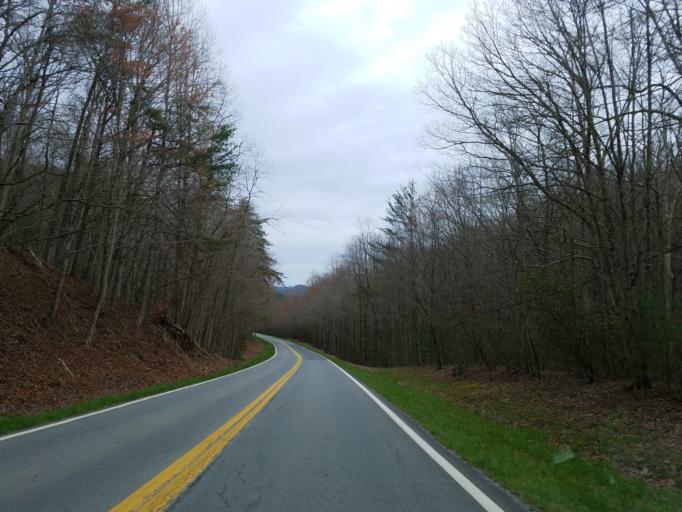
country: US
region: Georgia
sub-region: Fannin County
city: Blue Ridge
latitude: 34.8160
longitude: -84.2982
